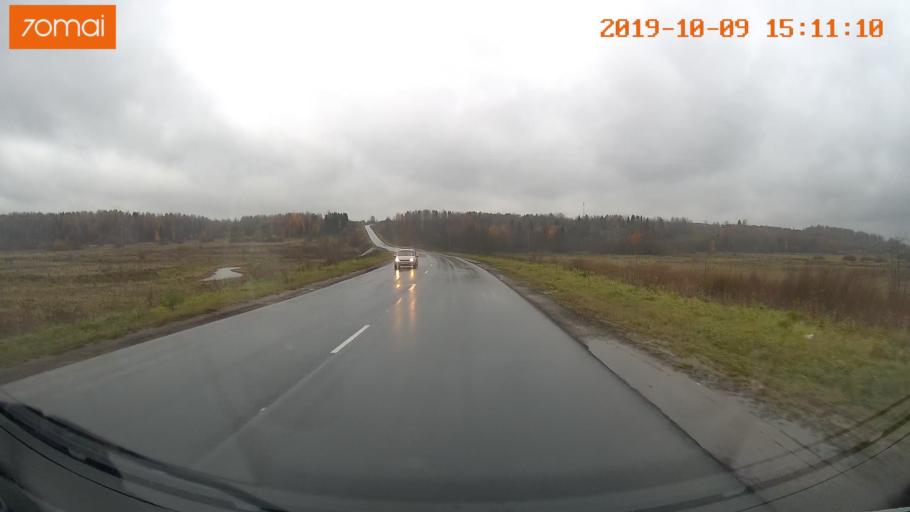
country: RU
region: Kostroma
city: Susanino
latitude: 58.1688
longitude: 41.6317
